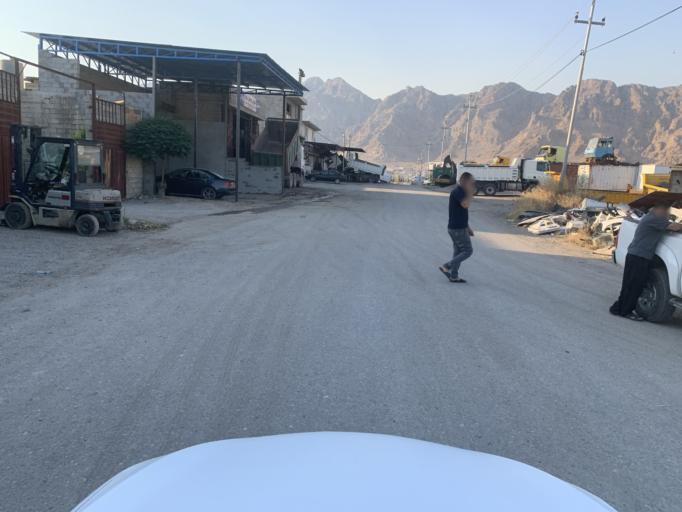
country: IQ
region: As Sulaymaniyah
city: Raniye
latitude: 36.2450
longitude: 44.8881
